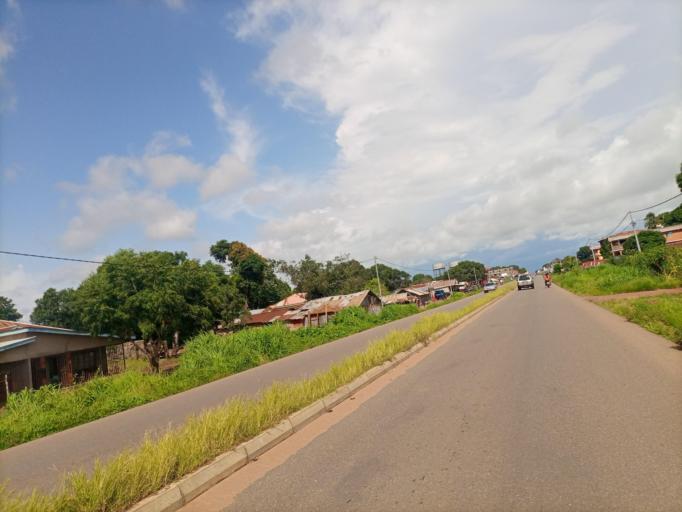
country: SL
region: Northern Province
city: Masoyila
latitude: 8.6071
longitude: -13.1833
